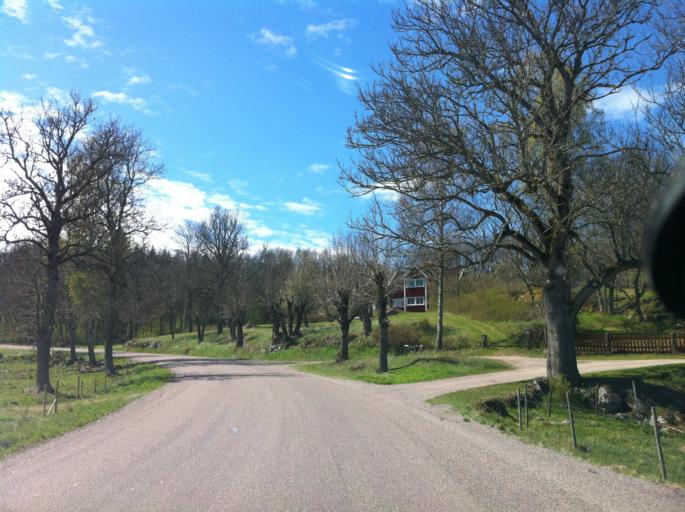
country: SE
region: Kalmar
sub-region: Vimmerby Kommun
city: Sodra Vi
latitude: 57.7689
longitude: 15.8442
